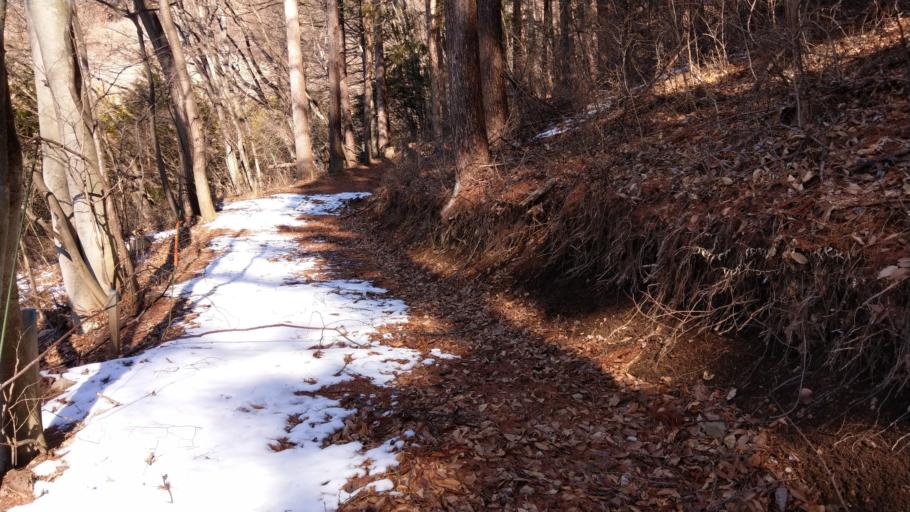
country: JP
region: Nagano
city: Komoro
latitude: 36.3601
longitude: 138.4404
